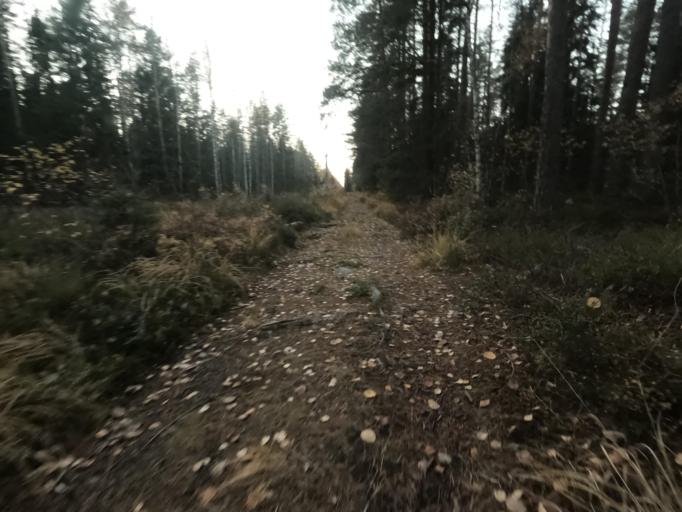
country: RU
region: St.-Petersburg
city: Komarovo
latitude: 60.2028
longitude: 29.8035
